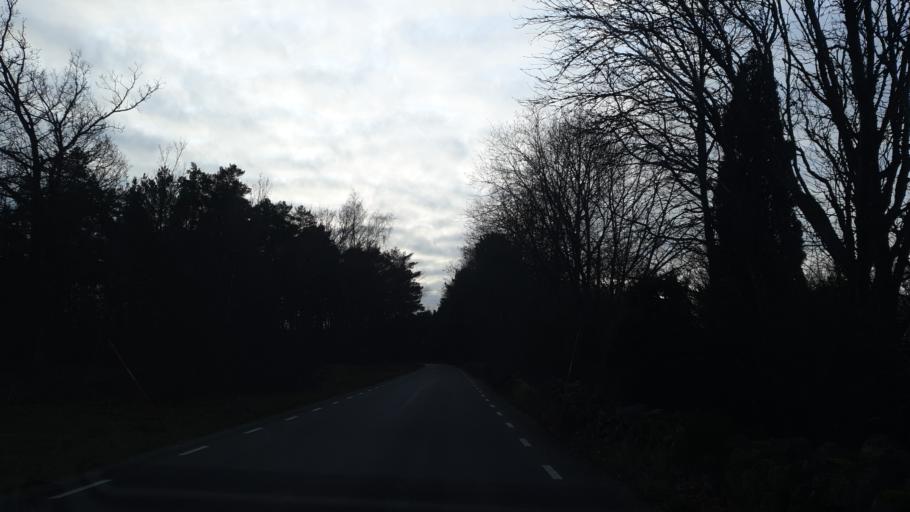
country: SE
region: Blekinge
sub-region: Karlskrona Kommun
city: Jaemjoe
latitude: 56.2237
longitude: 15.9880
